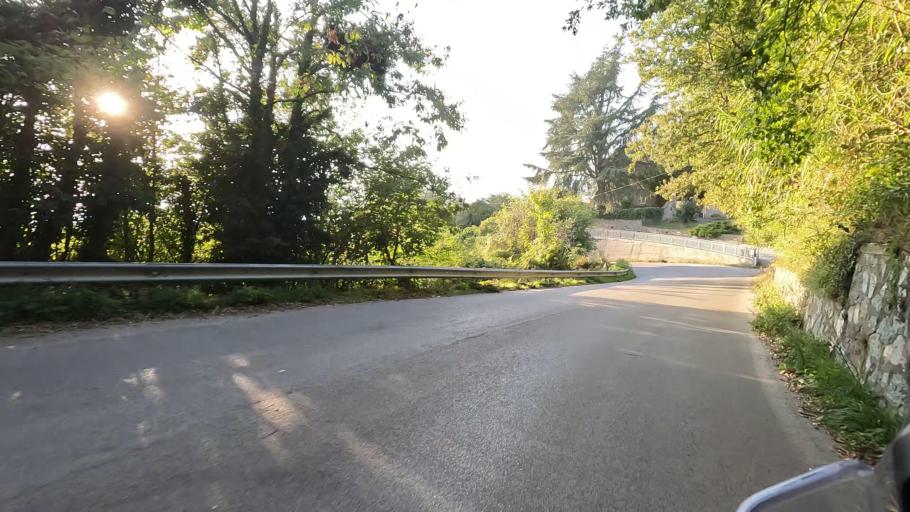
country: IT
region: Liguria
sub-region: Provincia di Savona
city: San Giovanni
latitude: 44.3987
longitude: 8.4960
